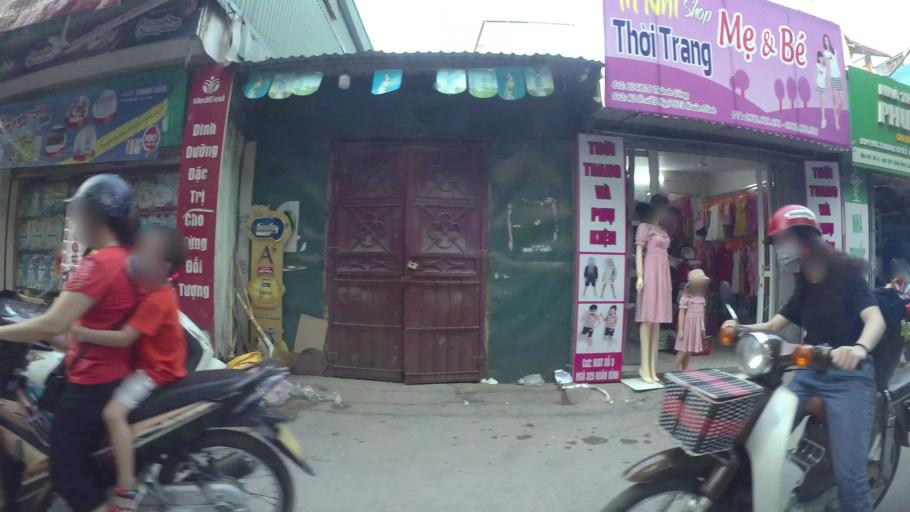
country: VN
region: Ha Noi
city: Tay Ho
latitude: 21.0696
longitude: 105.7916
